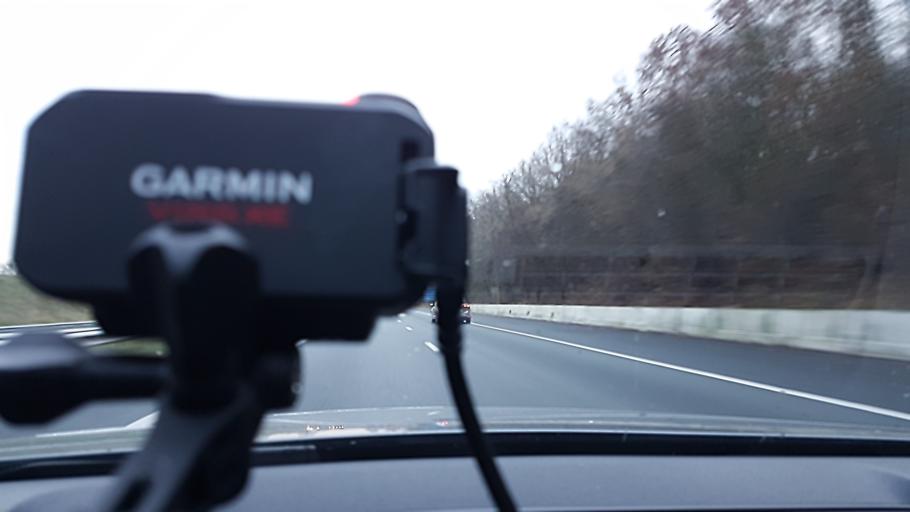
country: NL
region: Overijssel
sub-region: Gemeente Hengelo
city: Hengelo
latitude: 52.2816
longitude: 6.8115
